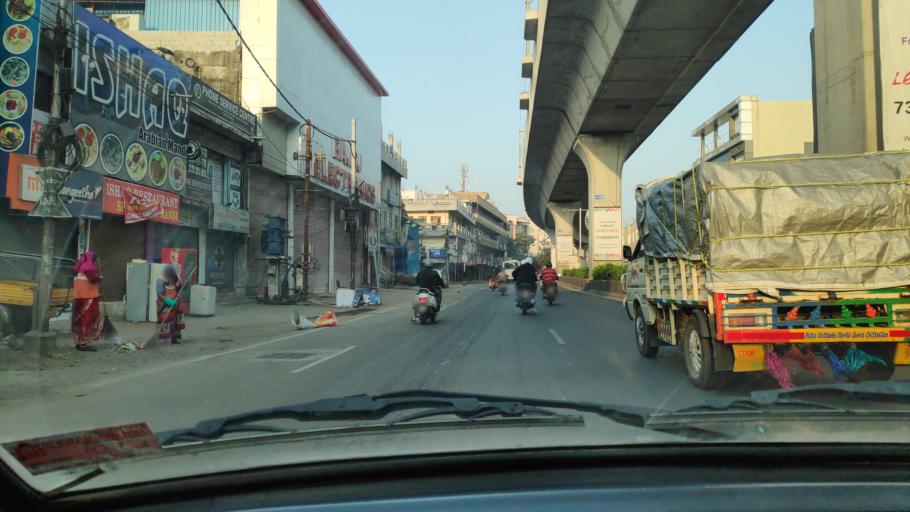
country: IN
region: Telangana
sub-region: Rangareddi
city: Gaddi Annaram
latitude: 17.3736
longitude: 78.5020
